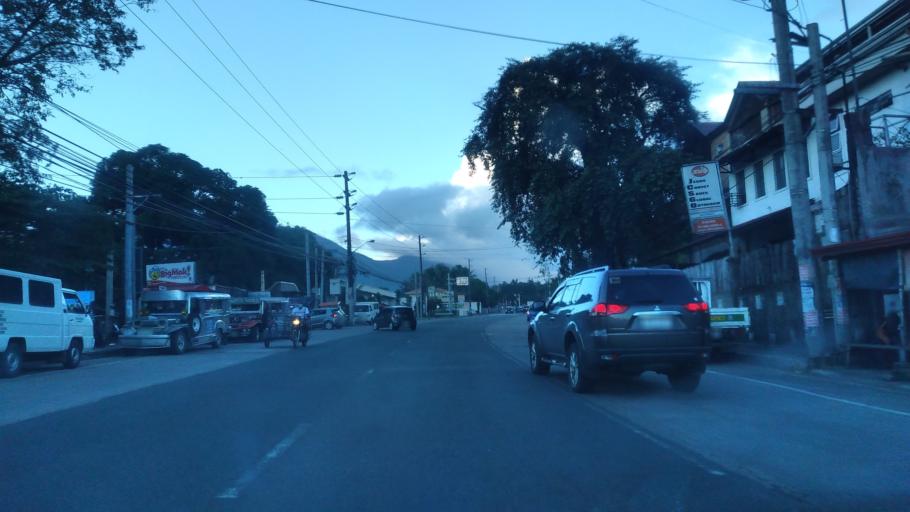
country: PH
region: Calabarzon
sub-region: Province of Quezon
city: Isabang
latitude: 13.9653
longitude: 121.5643
